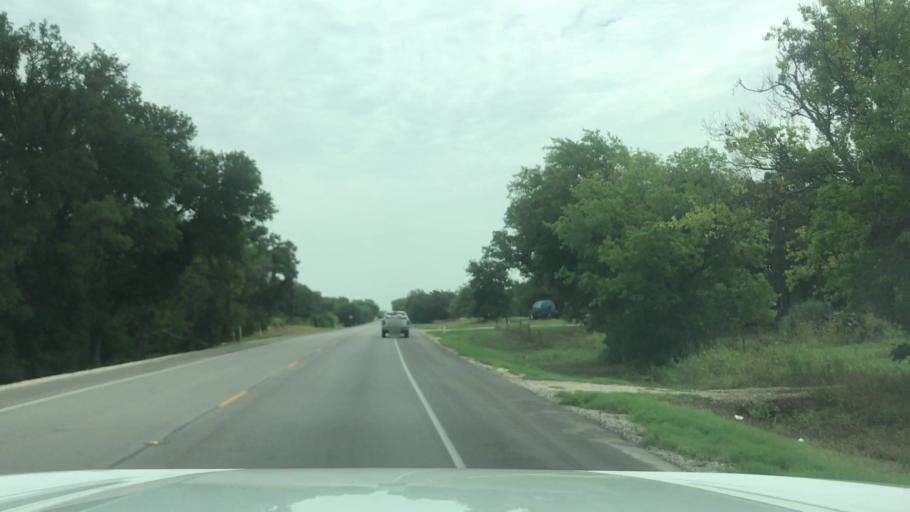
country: US
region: Texas
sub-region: Erath County
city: Dublin
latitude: 32.0880
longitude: -98.3029
